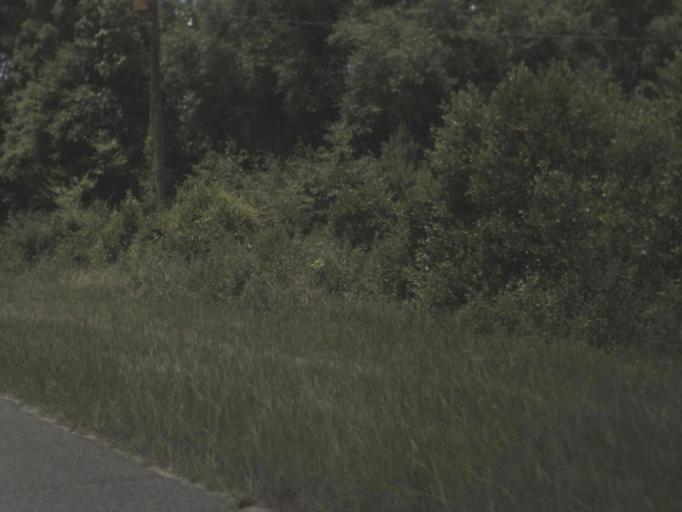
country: US
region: Florida
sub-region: Jefferson County
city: Monticello
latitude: 30.5607
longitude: -83.6374
